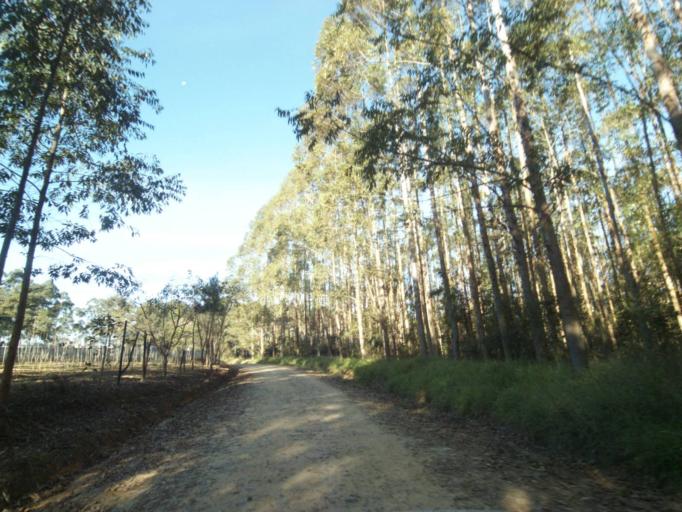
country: BR
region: Parana
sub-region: Telemaco Borba
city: Telemaco Borba
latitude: -24.5135
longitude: -50.6525
